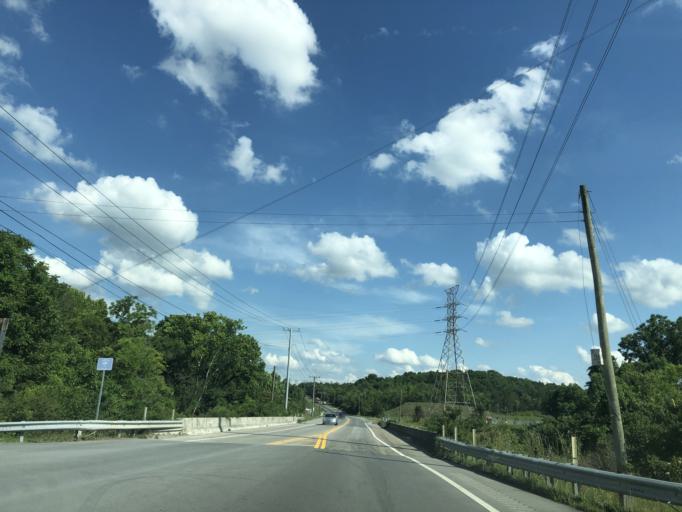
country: US
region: Tennessee
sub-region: Davidson County
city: Nashville
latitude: 36.2306
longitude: -86.8130
